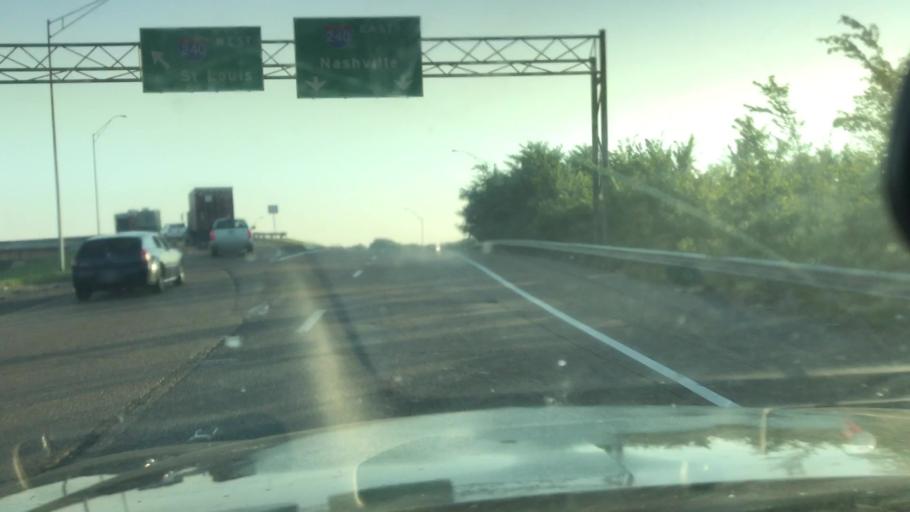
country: US
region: Tennessee
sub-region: Shelby County
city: New South Memphis
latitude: 35.0801
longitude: -89.9530
